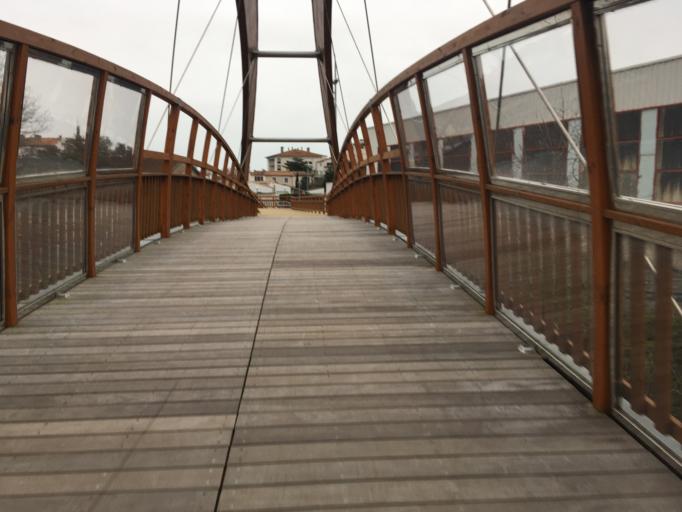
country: FR
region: Poitou-Charentes
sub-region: Departement de la Charente-Maritime
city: La Rochelle
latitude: 46.1666
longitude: -1.1442
